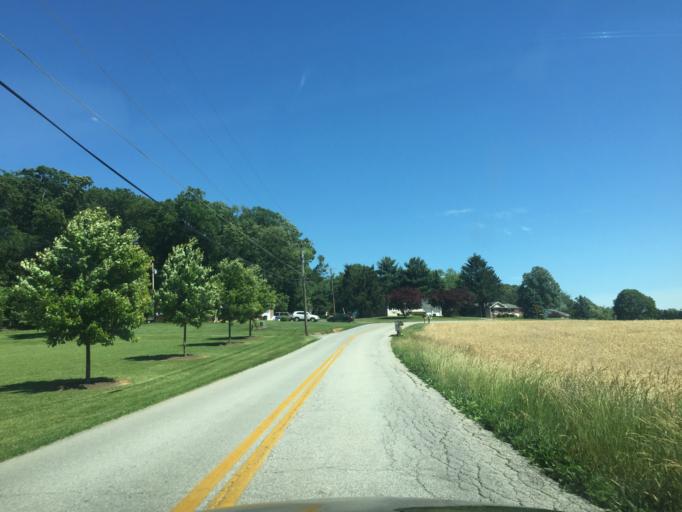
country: US
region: Maryland
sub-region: Carroll County
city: Manchester
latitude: 39.6270
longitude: -76.9311
